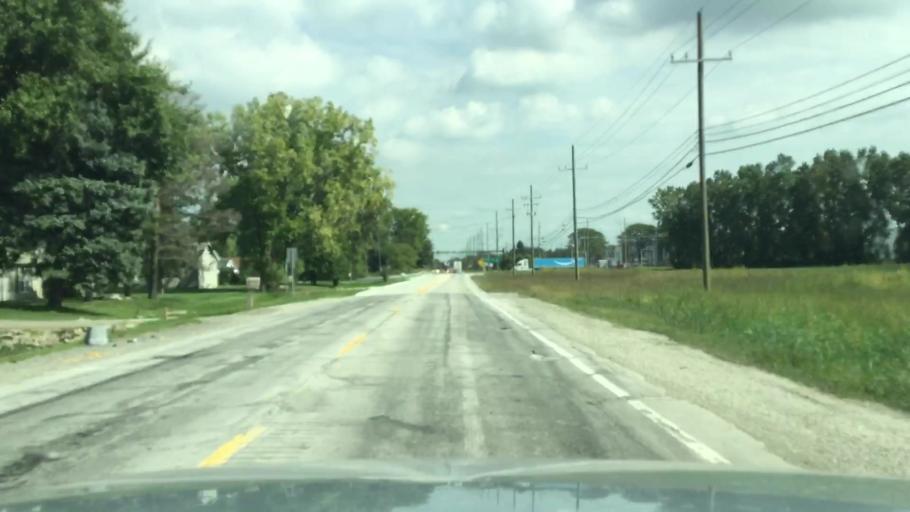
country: US
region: Michigan
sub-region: Wayne County
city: Wayne
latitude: 42.2524
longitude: -83.3702
